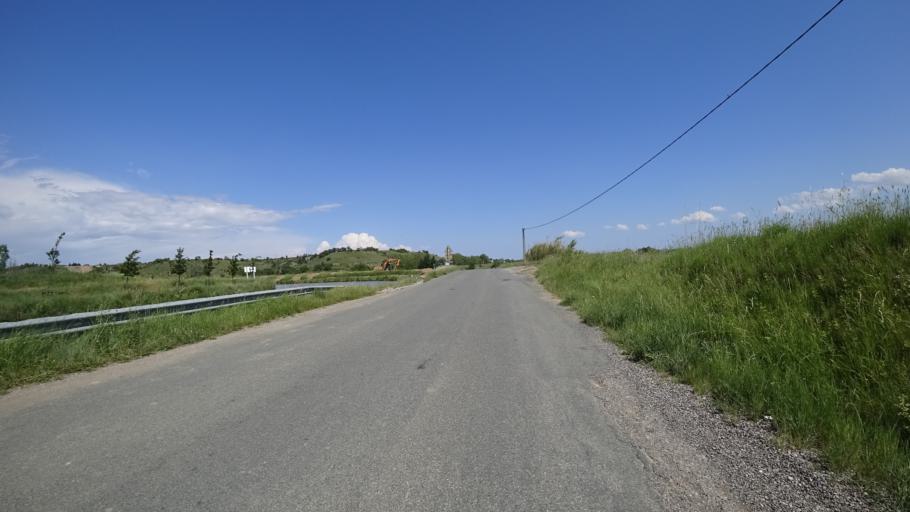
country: FR
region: Languedoc-Roussillon
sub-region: Departement de l'Aude
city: Canet
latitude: 43.2486
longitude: 2.8386
